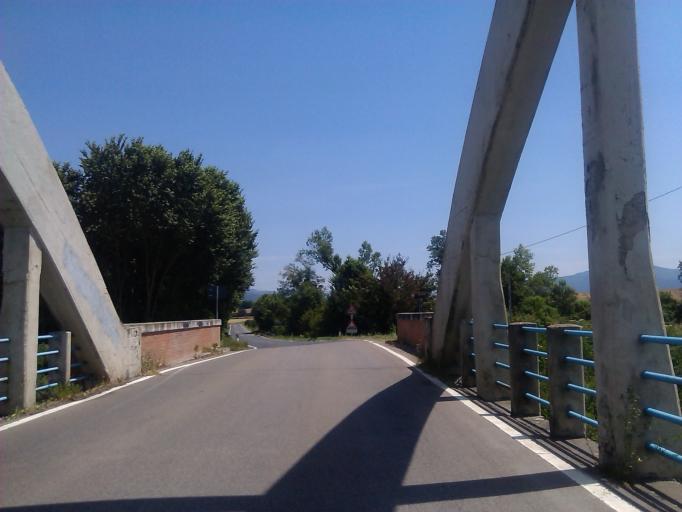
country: IT
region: Tuscany
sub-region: Province of Arezzo
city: Cesa
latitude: 43.3204
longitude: 11.8361
